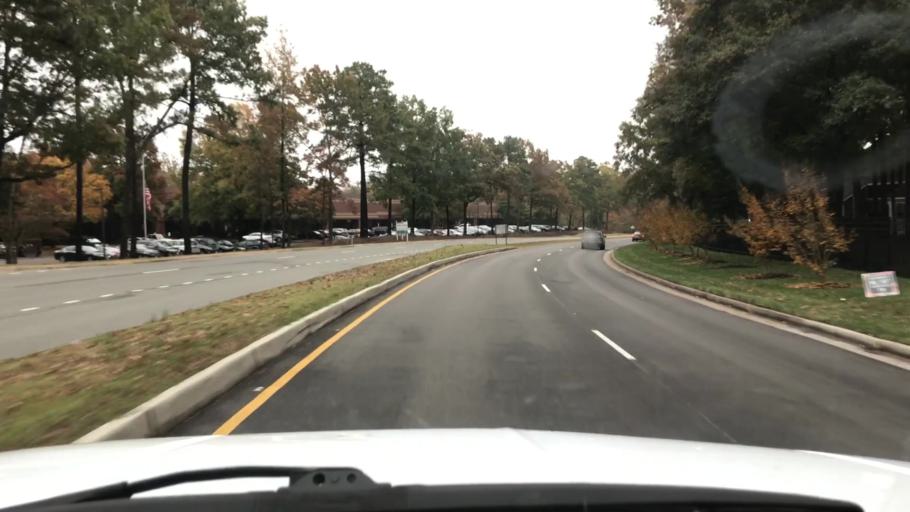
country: US
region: Virginia
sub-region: Henrico County
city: Lakeside
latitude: 37.6388
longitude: -77.4694
